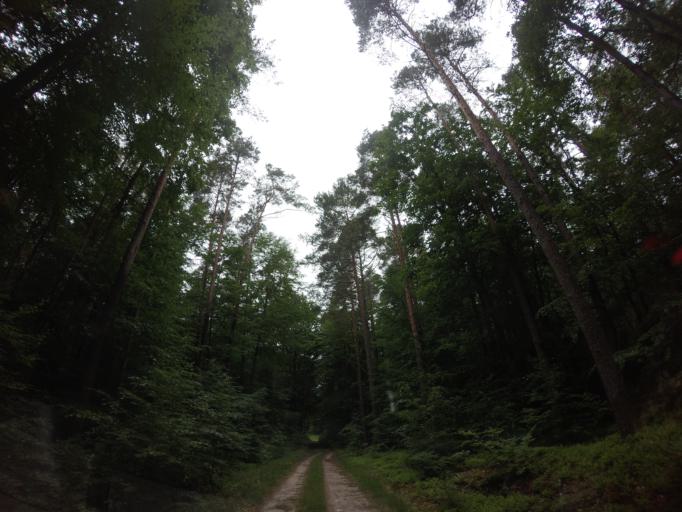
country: PL
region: West Pomeranian Voivodeship
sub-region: Powiat choszczenski
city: Drawno
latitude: 53.0994
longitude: 15.8291
